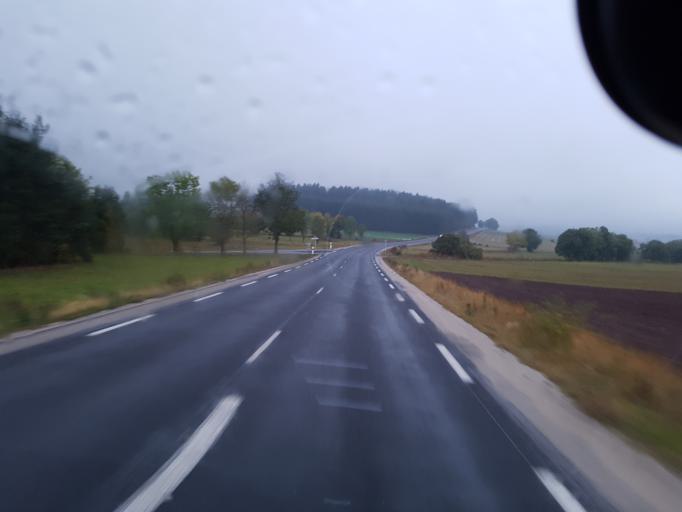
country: FR
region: Languedoc-Roussillon
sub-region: Departement de la Lozere
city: Langogne
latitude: 44.8256
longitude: 3.8709
